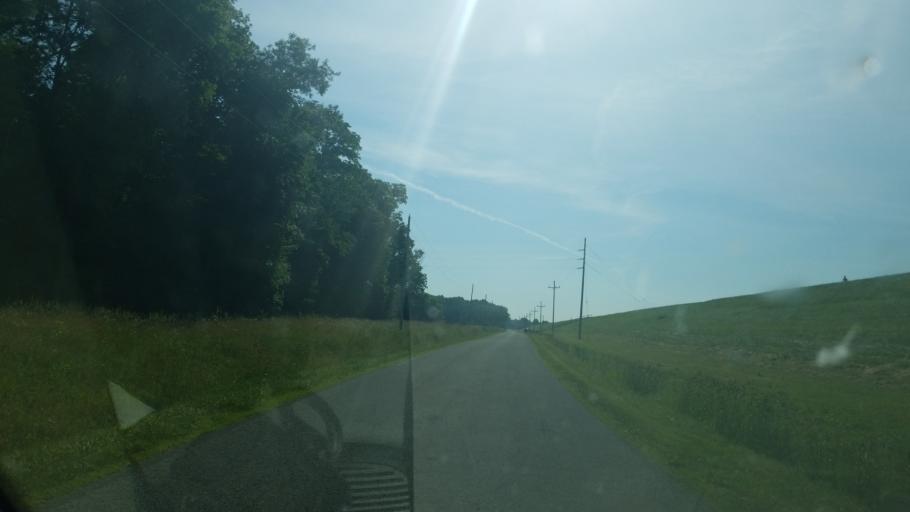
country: US
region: Ohio
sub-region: Hancock County
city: Findlay
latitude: 41.0290
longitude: -83.5789
